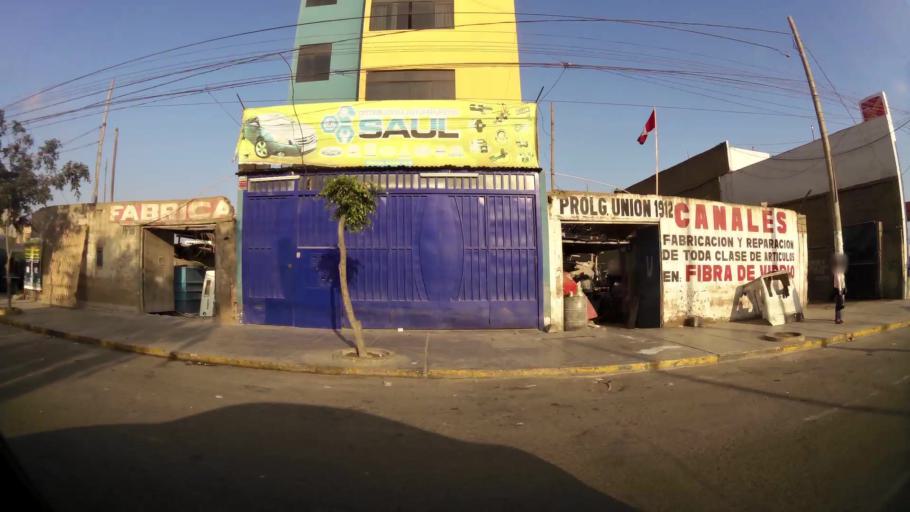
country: PE
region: La Libertad
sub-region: Provincia de Trujillo
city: El Porvenir
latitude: -8.0936
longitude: -79.0087
